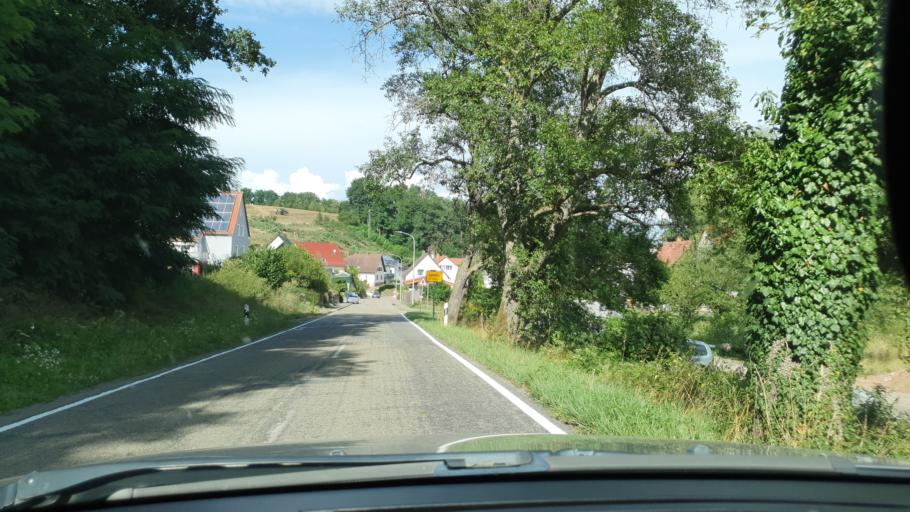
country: DE
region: Rheinland-Pfalz
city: Contwig
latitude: 49.2415
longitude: 7.4190
